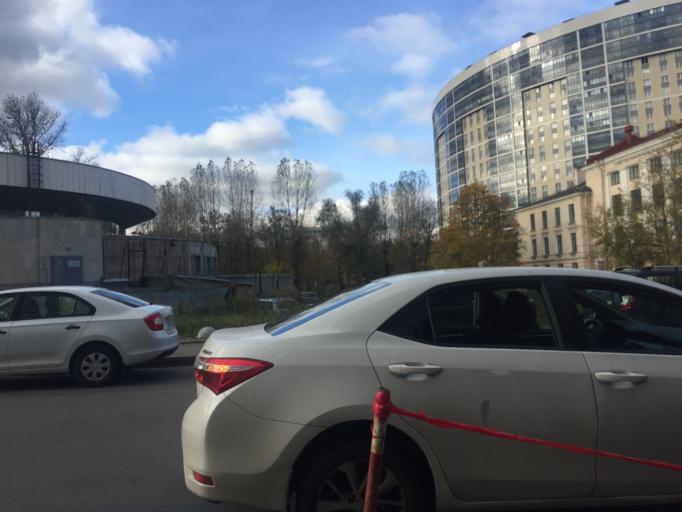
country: RU
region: St.-Petersburg
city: Obukhovo
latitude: 59.8652
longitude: 30.4711
